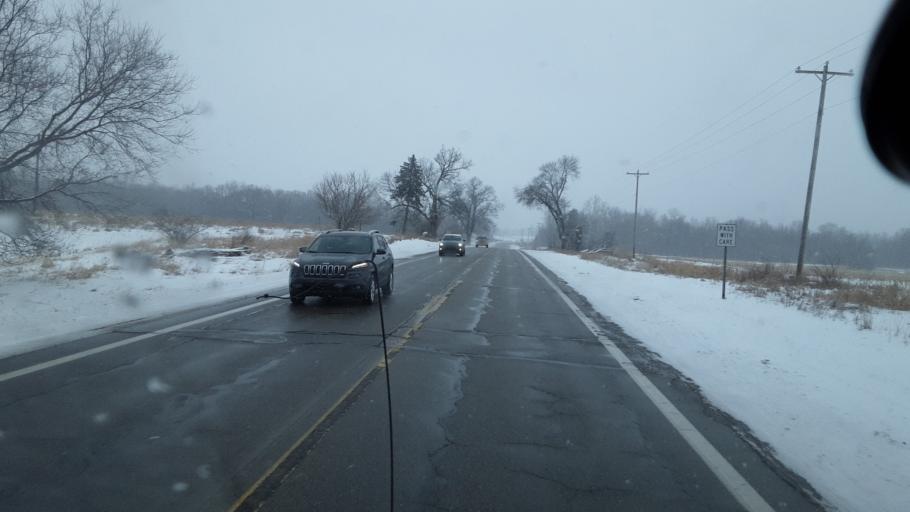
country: US
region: Michigan
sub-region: Jackson County
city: Jackson
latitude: 42.3073
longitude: -84.3890
